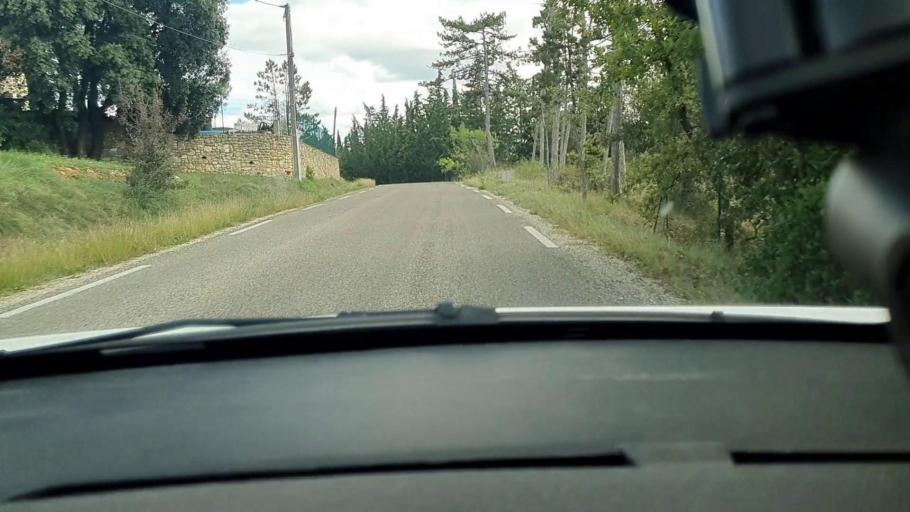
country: FR
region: Languedoc-Roussillon
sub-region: Departement du Gard
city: Les Mages
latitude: 44.2145
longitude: 4.1846
